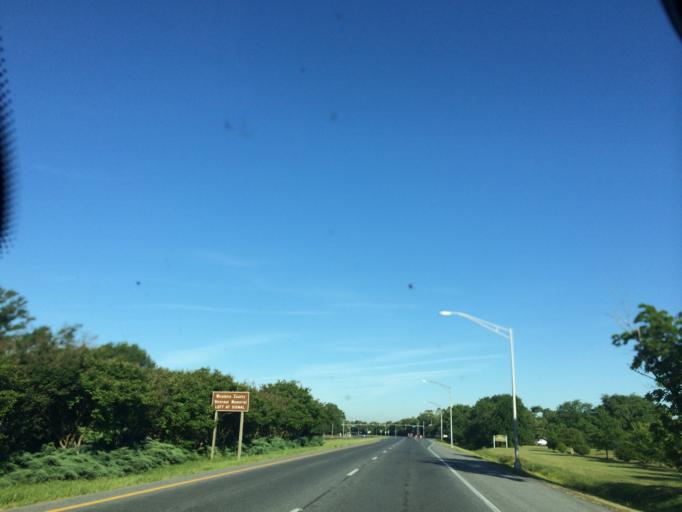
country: US
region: Maryland
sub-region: Wicomico County
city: Salisbury
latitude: 38.3686
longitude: -75.5697
